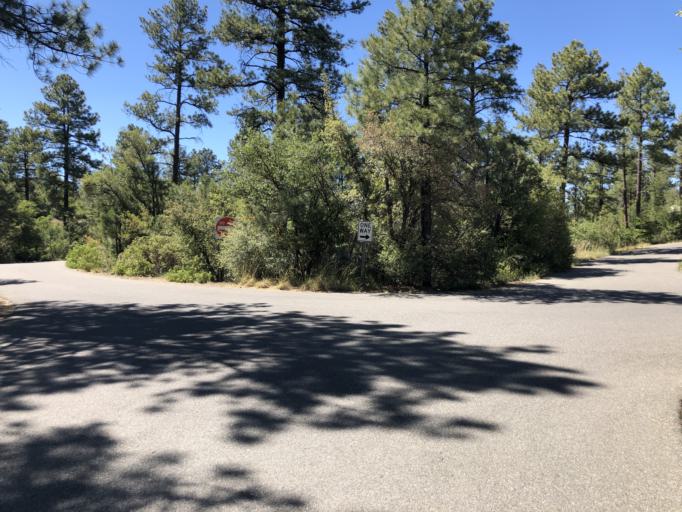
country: US
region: Arizona
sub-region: Yavapai County
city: Prescott
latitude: 34.5153
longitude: -112.3899
